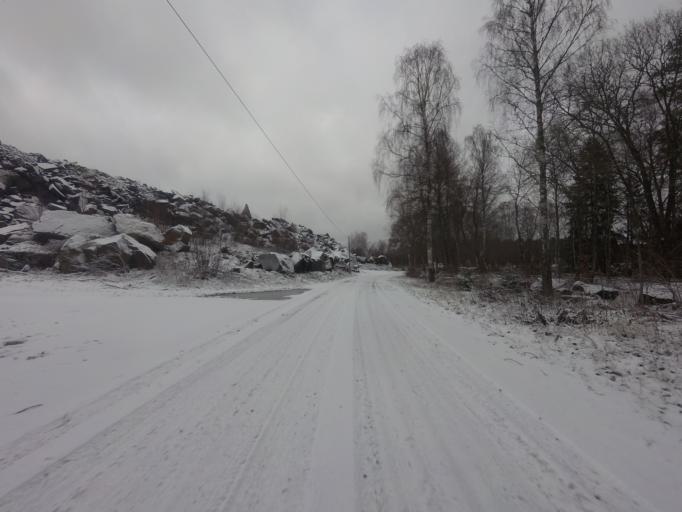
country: SE
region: Skane
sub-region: Osby Kommun
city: Lonsboda
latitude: 56.3974
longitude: 14.2507
